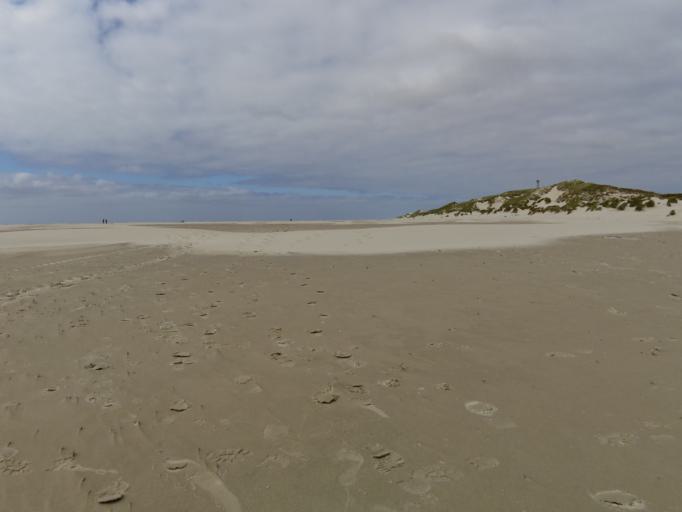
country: DE
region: Schleswig-Holstein
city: Nebel
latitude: 54.6234
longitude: 8.3546
